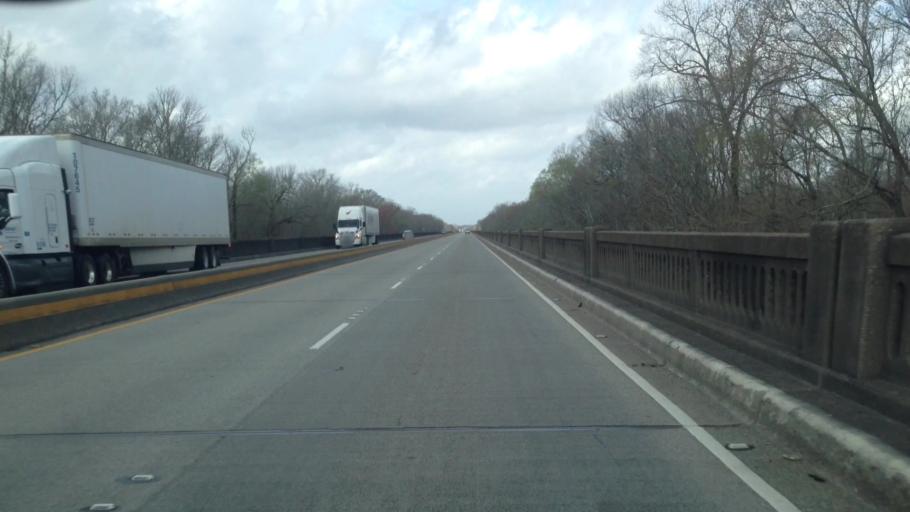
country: US
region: Louisiana
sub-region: Saint Landry Parish
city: Krotz Springs
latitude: 30.5536
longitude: -91.7032
